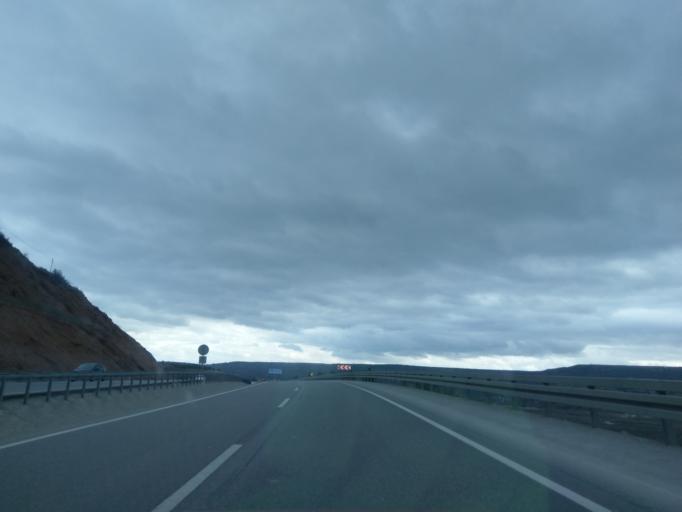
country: TR
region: Kuetahya
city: Sabuncu
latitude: 39.5744
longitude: 30.0960
